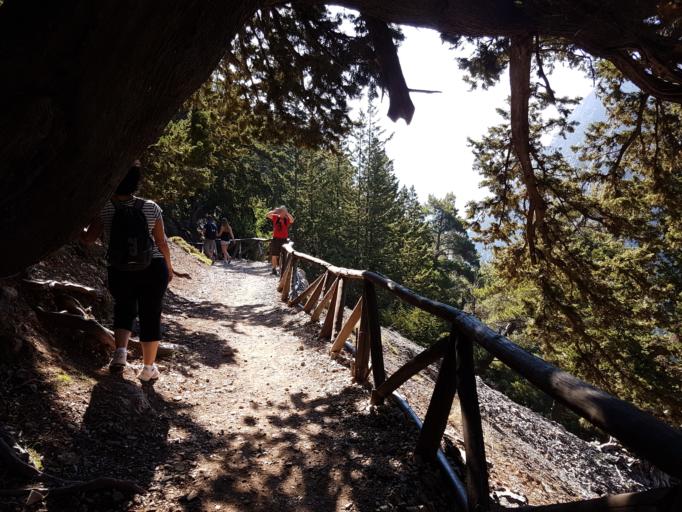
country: GR
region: Crete
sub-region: Nomos Chanias
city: Perivolia
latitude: 35.3076
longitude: 23.9197
